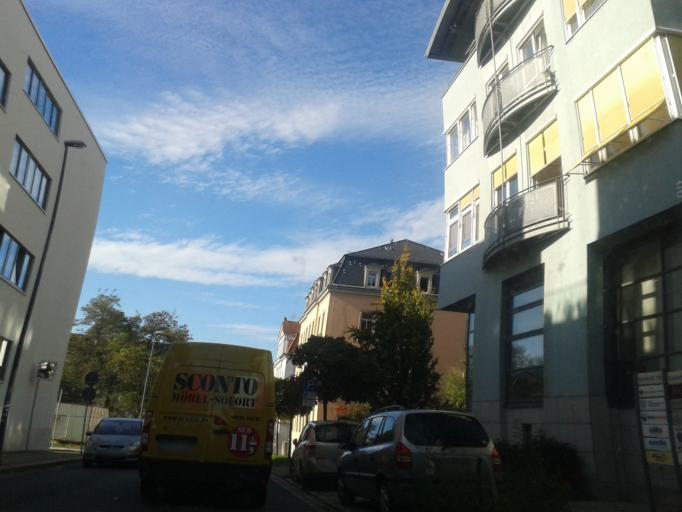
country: DE
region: Saxony
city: Albertstadt
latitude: 51.0778
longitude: 13.7493
